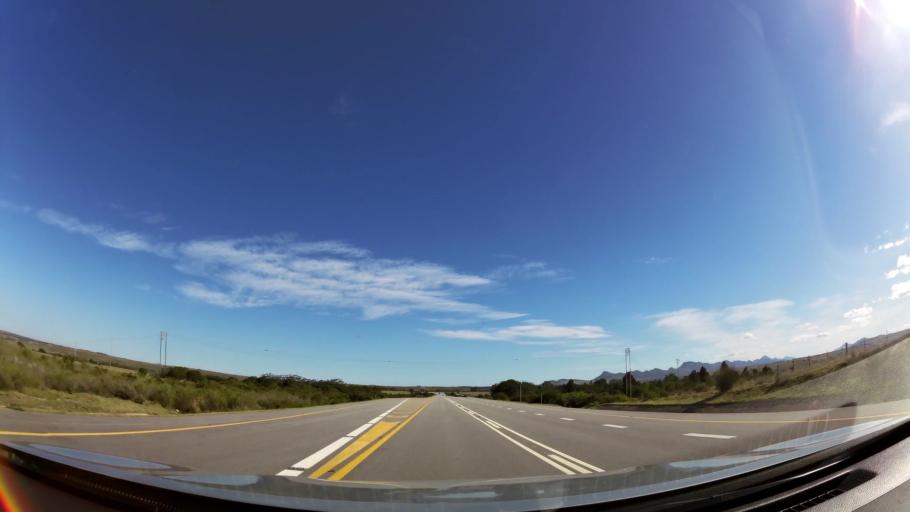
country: ZA
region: Eastern Cape
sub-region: Cacadu District Municipality
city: Kruisfontein
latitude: -34.0266
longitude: 24.6052
